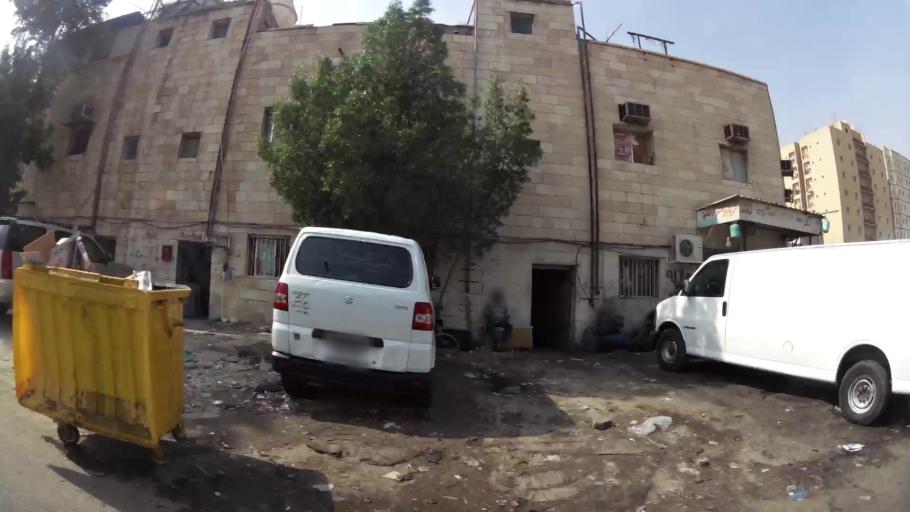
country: KW
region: Al Farwaniyah
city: Al Farwaniyah
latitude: 29.2550
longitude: 47.9458
